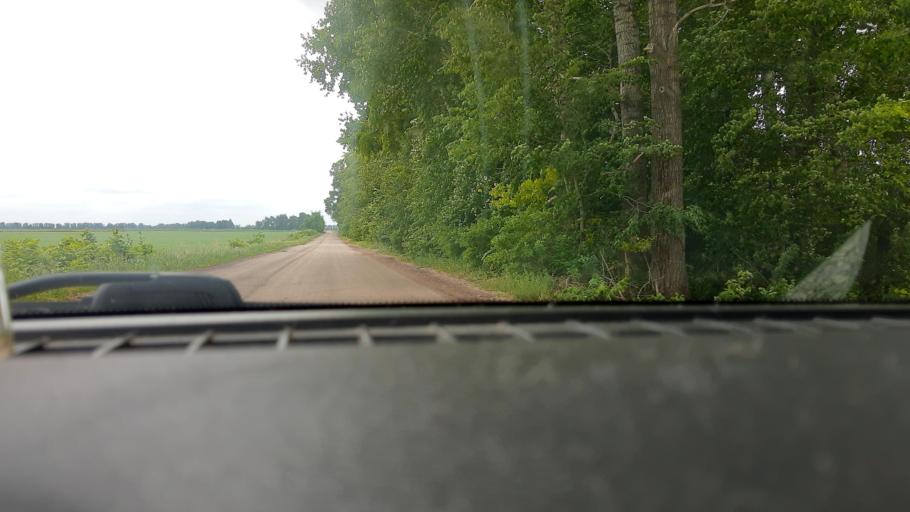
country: RU
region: Bashkortostan
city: Asanovo
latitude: 54.7560
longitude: 55.4972
